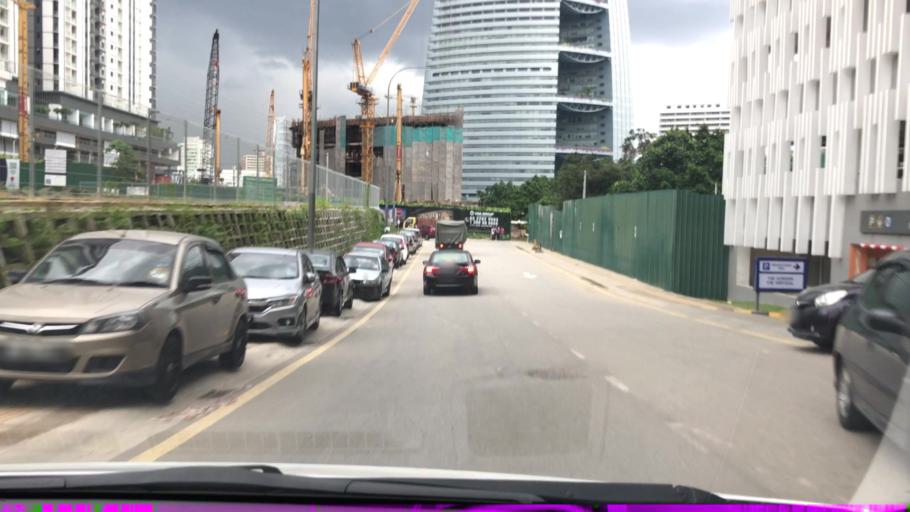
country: MY
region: Kuala Lumpur
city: Kuala Lumpur
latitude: 3.1121
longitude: 101.6655
